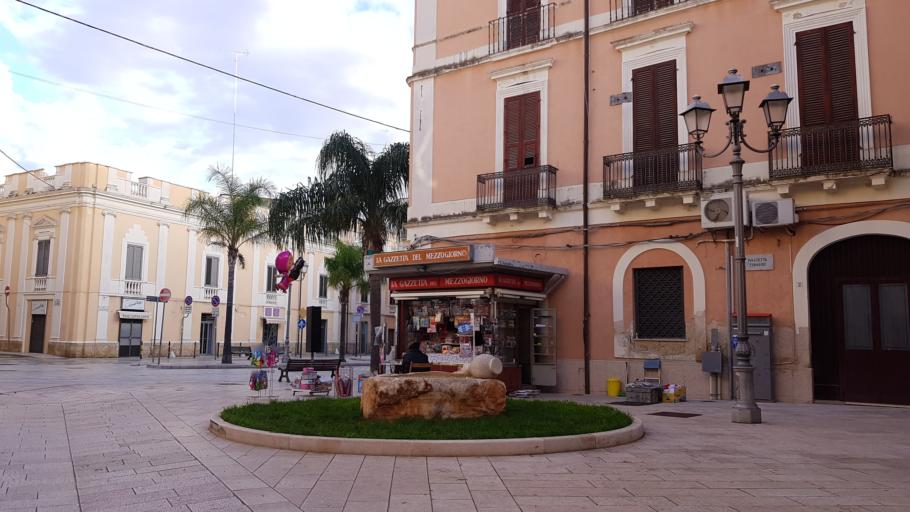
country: IT
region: Apulia
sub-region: Provincia di Brindisi
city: Brindisi
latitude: 40.6360
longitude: 17.9440
